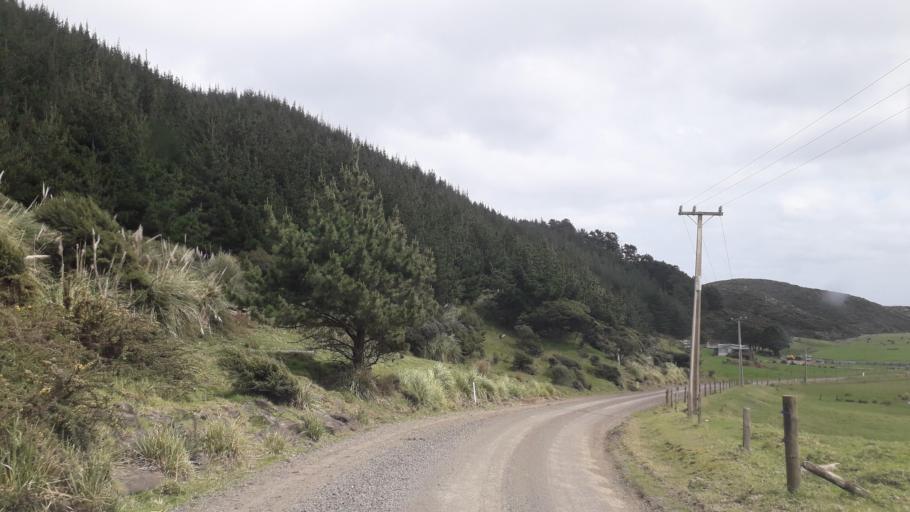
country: NZ
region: Northland
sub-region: Far North District
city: Ahipara
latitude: -35.4411
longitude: 173.2998
